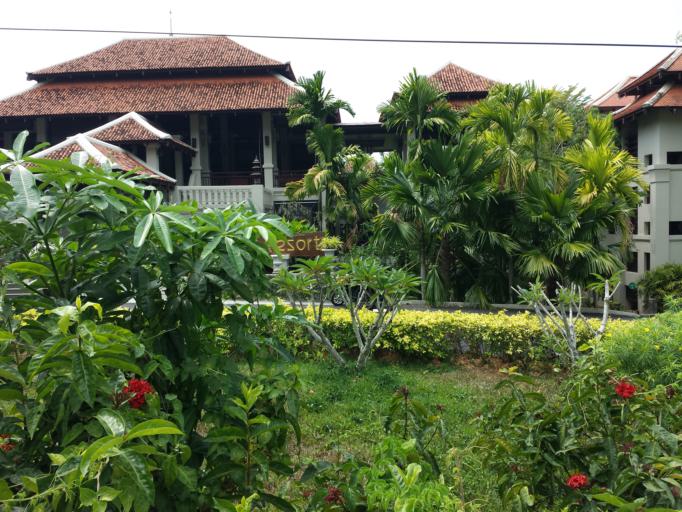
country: TH
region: Phangnga
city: Ban Khao Lak
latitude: 8.6380
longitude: 98.2483
